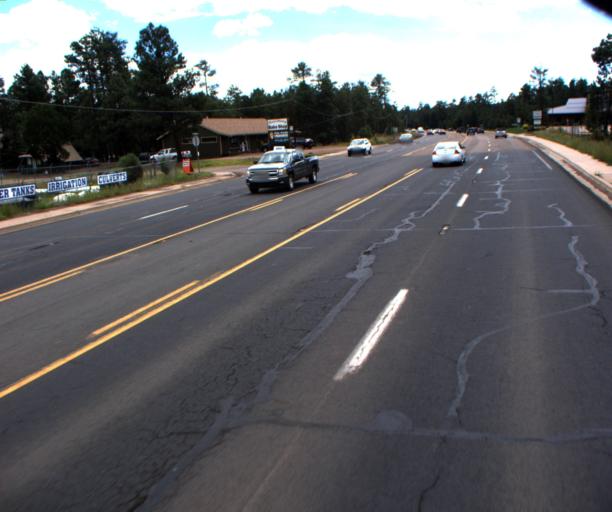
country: US
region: Arizona
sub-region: Navajo County
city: Lake of the Woods
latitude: 34.1857
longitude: -110.0156
